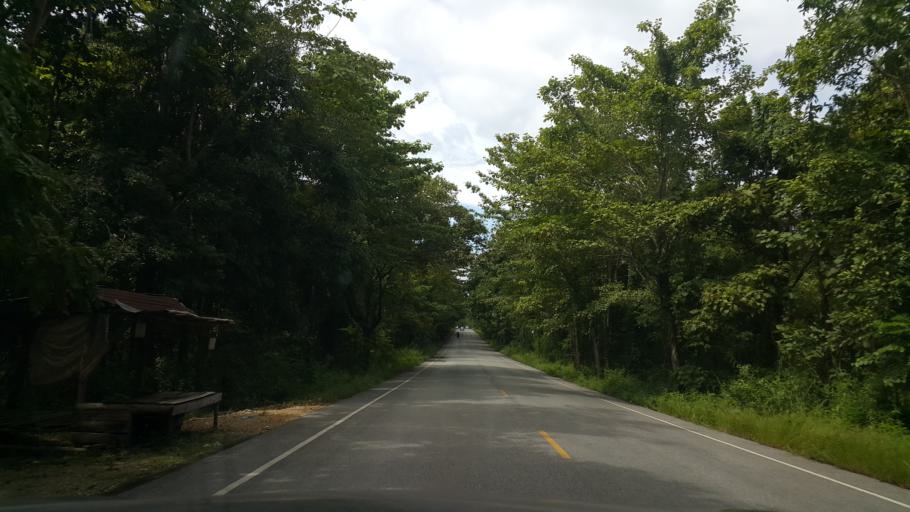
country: TH
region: Sukhothai
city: Thung Saliam
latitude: 17.4259
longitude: 99.3786
